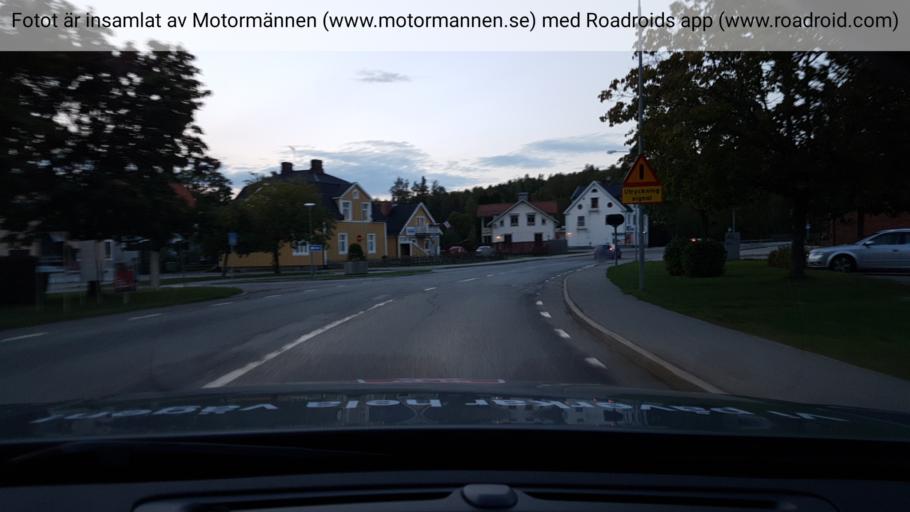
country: SE
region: OErebro
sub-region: Ljusnarsbergs Kommun
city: Kopparberg
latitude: 59.8734
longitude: 14.9874
